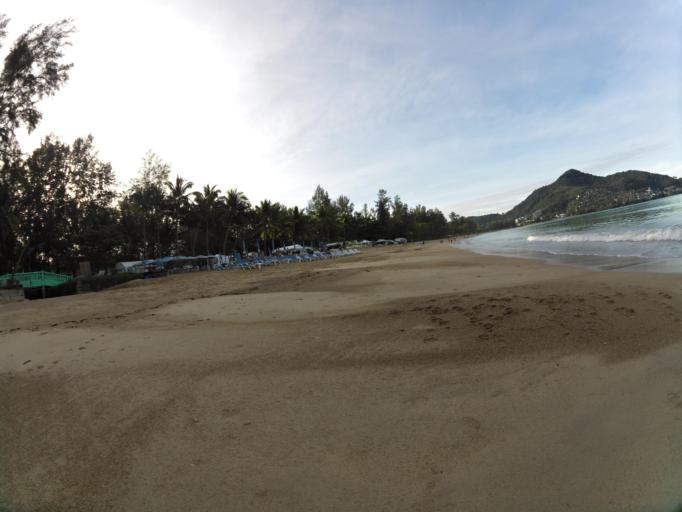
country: TH
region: Phuket
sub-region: Amphoe Kathu
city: Kathu
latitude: 7.9605
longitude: 98.2835
